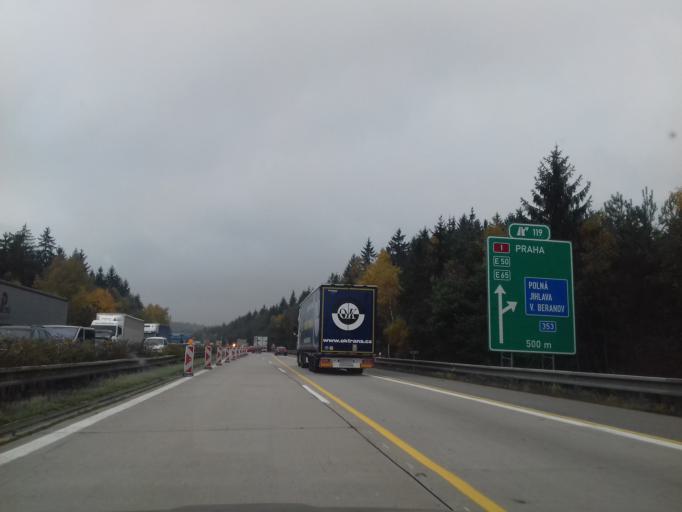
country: CZ
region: Vysocina
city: Velky Beranov
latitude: 49.4207
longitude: 15.6978
